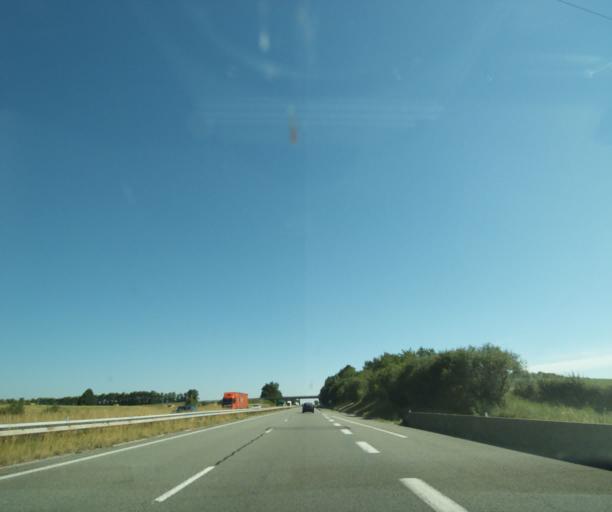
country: FR
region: Champagne-Ardenne
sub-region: Departement de la Haute-Marne
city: Avrecourt
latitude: 47.9971
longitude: 5.5143
